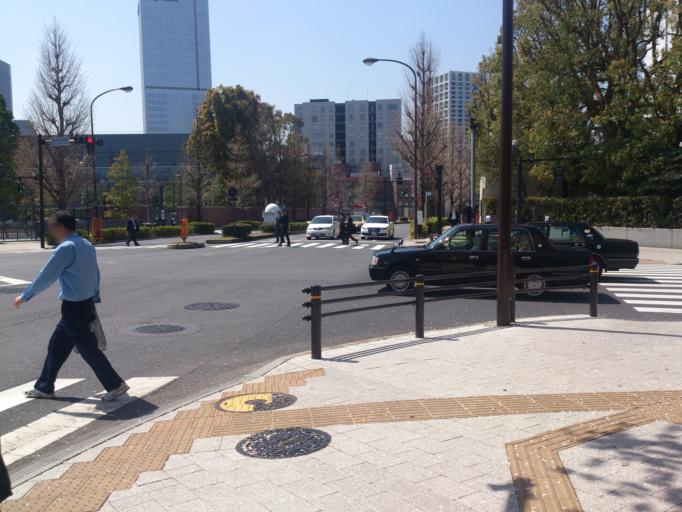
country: JP
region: Tokyo
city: Tokyo
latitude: 35.6778
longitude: 139.7434
